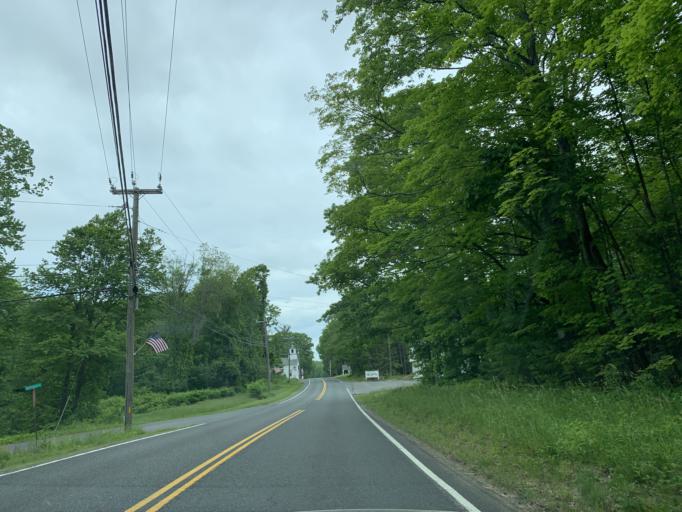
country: US
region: Massachusetts
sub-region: Hampshire County
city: Southampton
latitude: 42.2121
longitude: -72.8160
